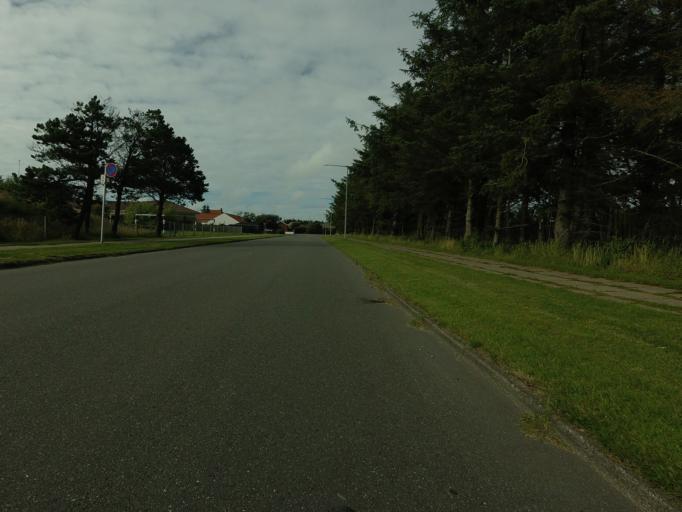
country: DK
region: North Denmark
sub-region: Jammerbugt Kommune
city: Pandrup
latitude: 57.3677
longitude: 9.7176
